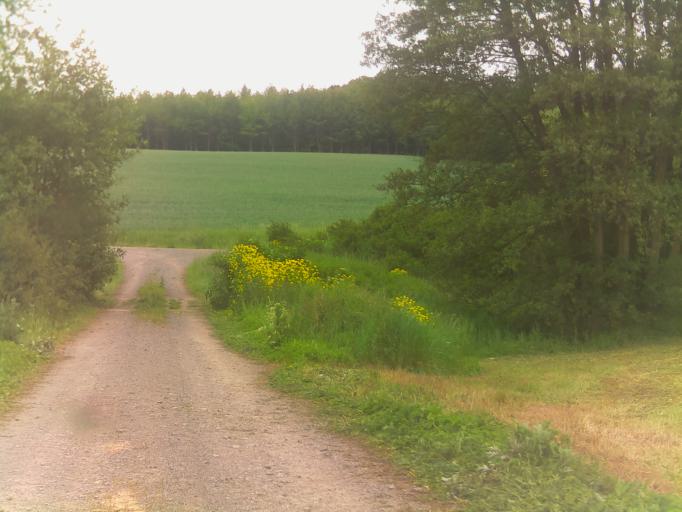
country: DE
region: Thuringia
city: Henneberg
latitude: 50.4486
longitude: 10.3691
